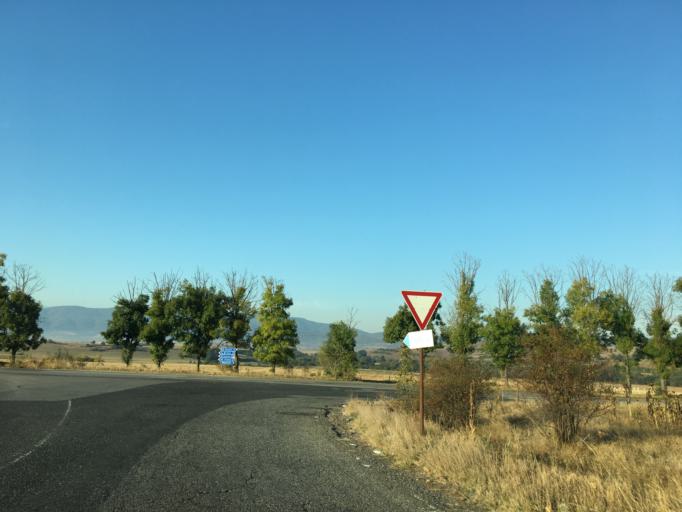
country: BG
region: Sofiya
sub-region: Obshtina Ikhtiman
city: Ikhtiman
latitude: 42.4849
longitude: 23.7845
